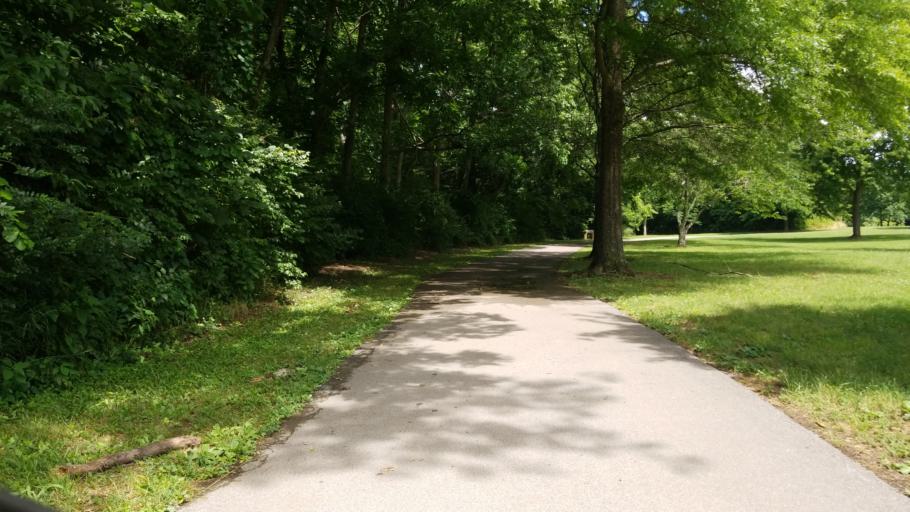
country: US
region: Tennessee
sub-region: Davidson County
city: Forest Hills
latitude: 36.0367
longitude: -86.8403
